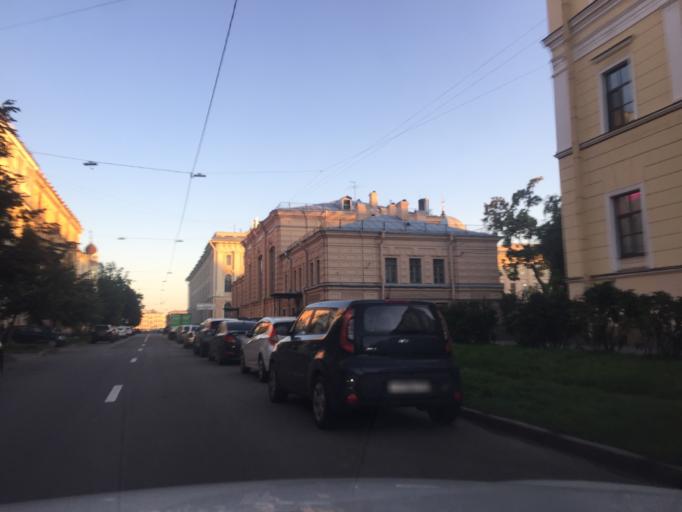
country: RU
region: St.-Petersburg
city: Saint Petersburg
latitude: 59.9398
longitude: 30.2893
